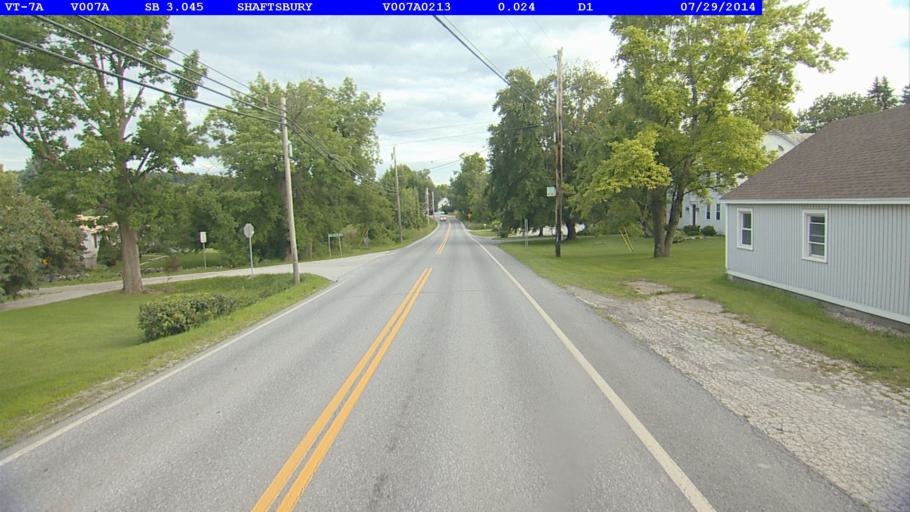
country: US
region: Vermont
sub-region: Bennington County
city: North Bennington
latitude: 42.9330
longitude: -73.2101
